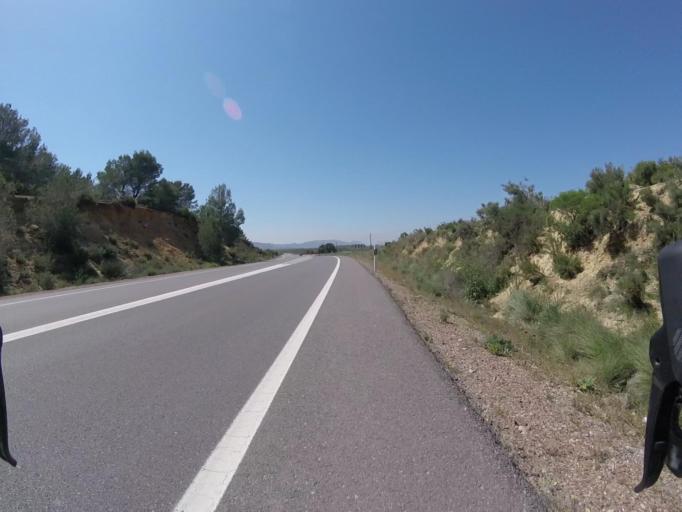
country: ES
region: Valencia
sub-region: Provincia de Castello
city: Benlloch
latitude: 40.2202
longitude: 0.0476
